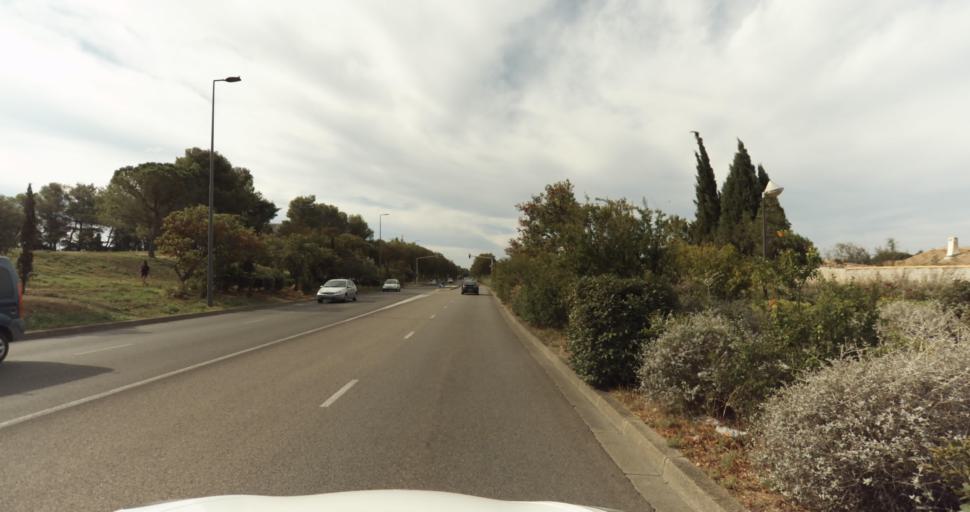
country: FR
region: Provence-Alpes-Cote d'Azur
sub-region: Departement des Bouches-du-Rhone
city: Miramas
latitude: 43.5957
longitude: 5.0050
